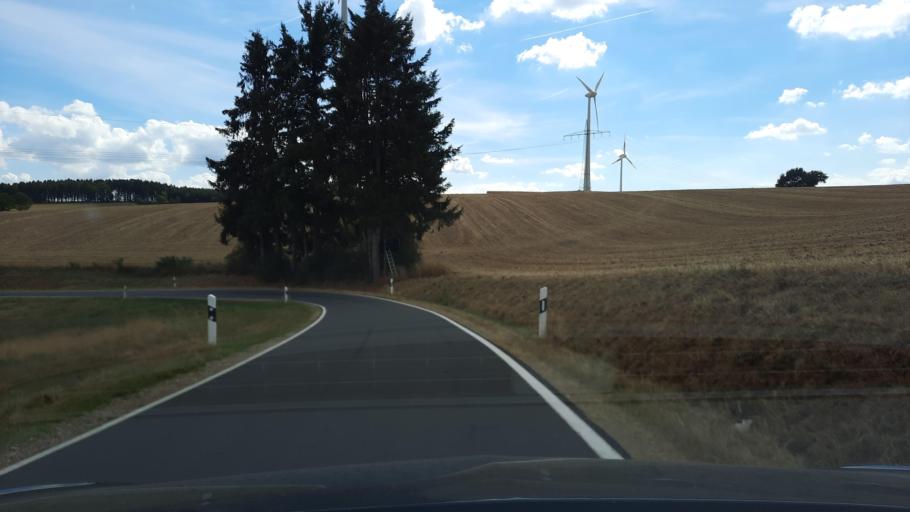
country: DE
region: Rheinland-Pfalz
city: Pronsfeld
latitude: 50.1796
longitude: 6.3281
